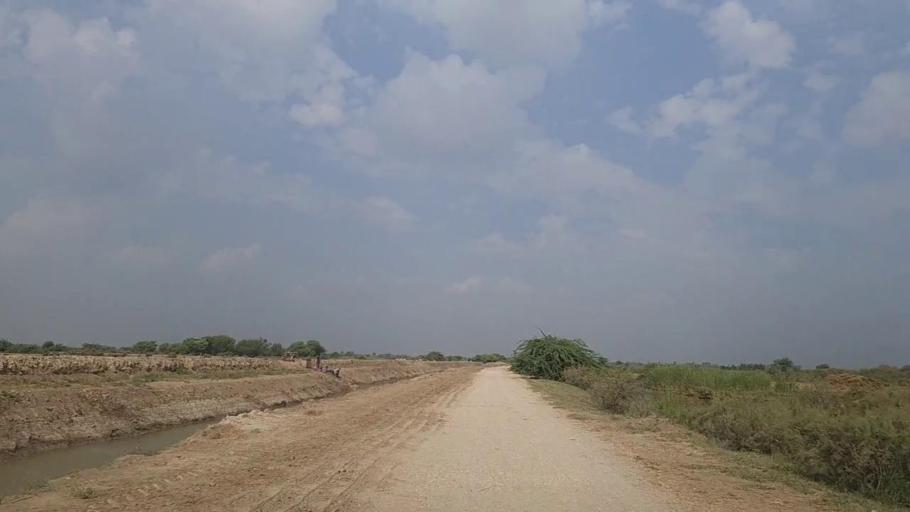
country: PK
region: Sindh
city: Daro Mehar
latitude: 24.6951
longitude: 68.1267
